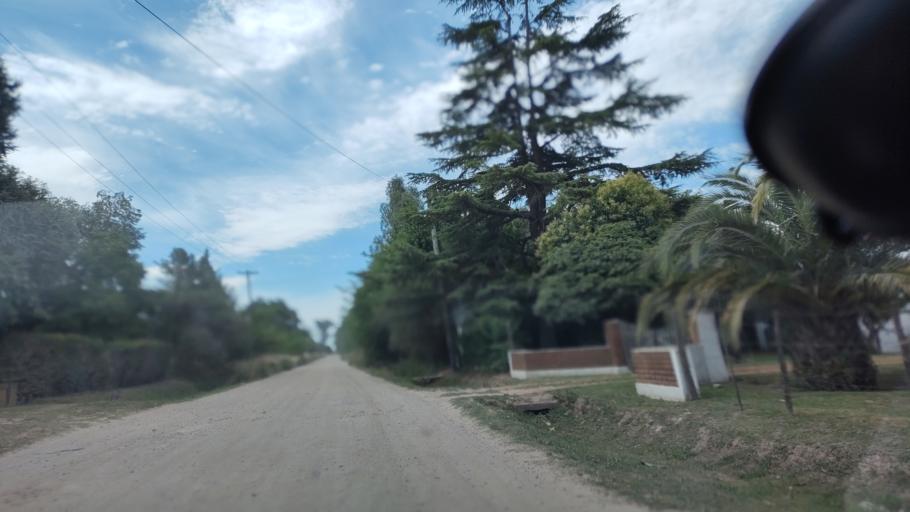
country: AR
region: Buenos Aires
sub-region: Partido de Lobos
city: Lobos
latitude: -35.1772
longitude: -59.1085
